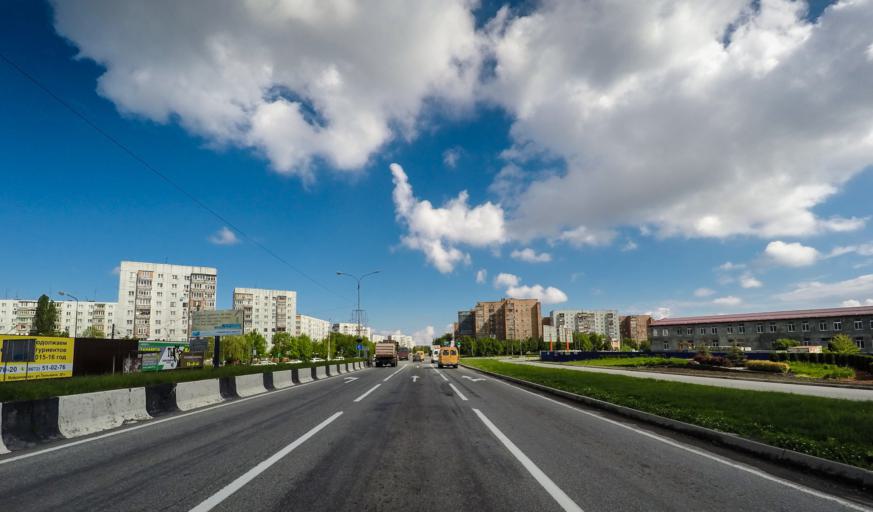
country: RU
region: North Ossetia
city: Vladikavkaz
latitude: 43.0357
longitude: 44.6415
